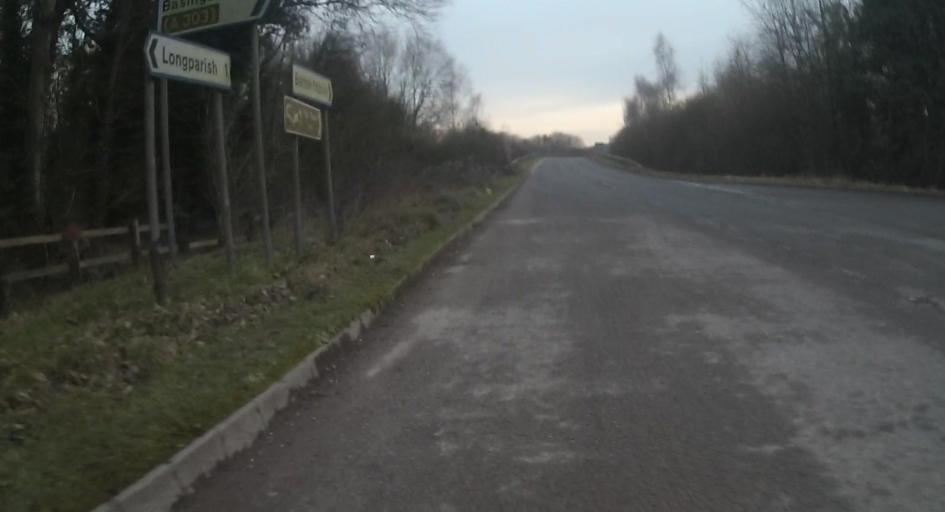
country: GB
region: England
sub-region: Hampshire
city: Kings Worthy
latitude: 51.1821
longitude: -1.3743
